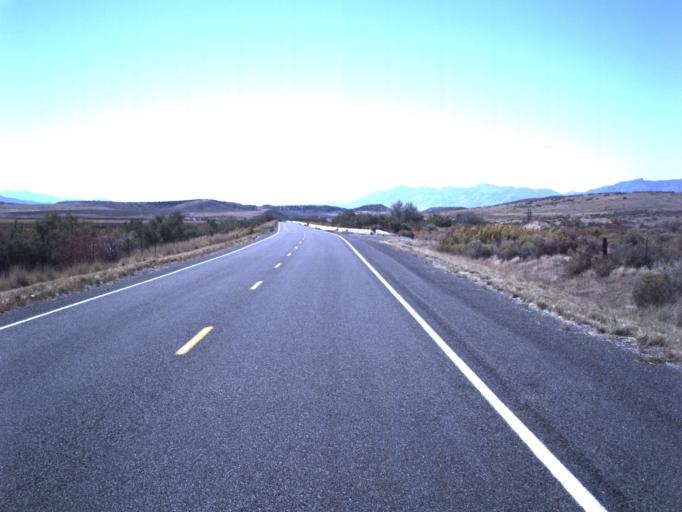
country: US
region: Utah
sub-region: Juab County
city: Nephi
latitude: 39.4984
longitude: -111.9602
